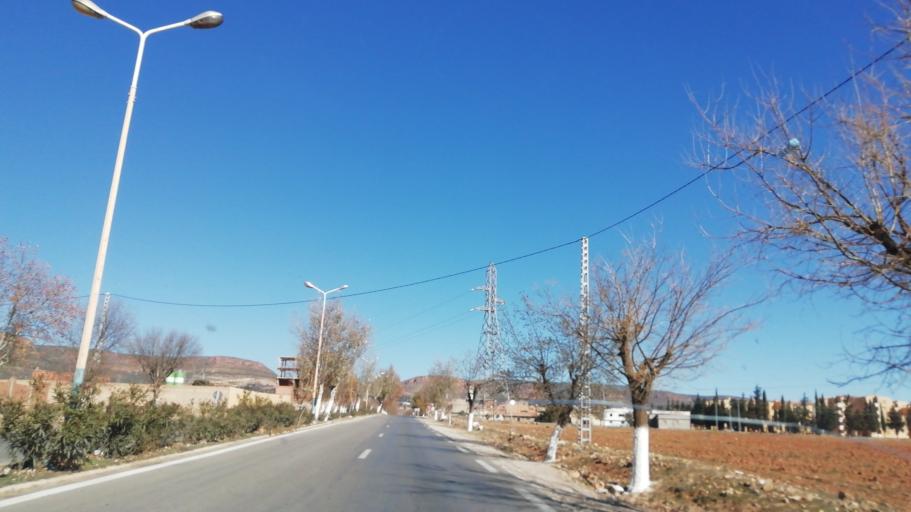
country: DZ
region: Tlemcen
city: Sebdou
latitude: 34.6610
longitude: -1.3230
